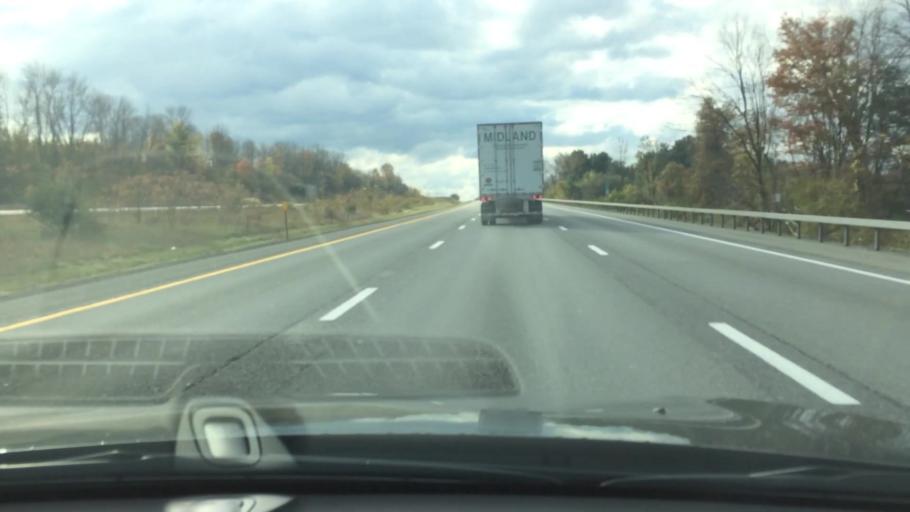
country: US
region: New York
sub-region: Saratoga County
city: Ballston Spa
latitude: 42.9931
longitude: -73.8040
